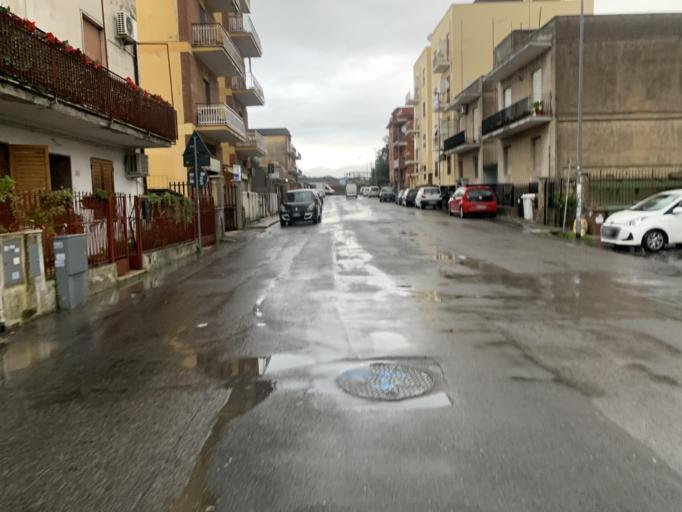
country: IT
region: Latium
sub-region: Citta metropolitana di Roma Capitale
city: Setteville
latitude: 41.9443
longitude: 12.6525
